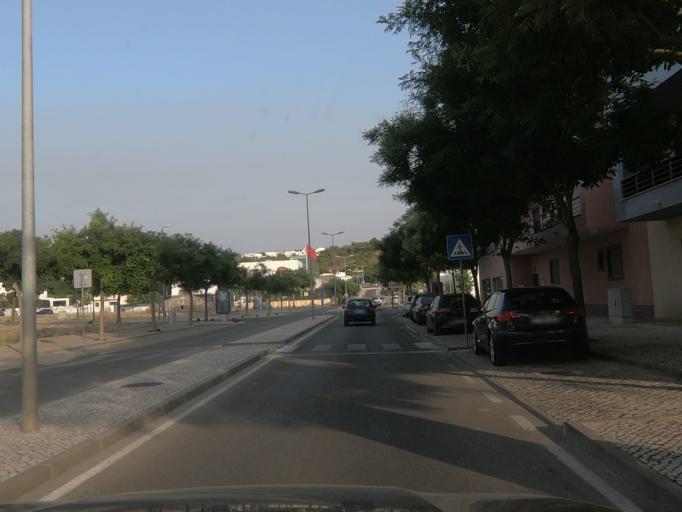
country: PT
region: Faro
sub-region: Loule
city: Loule
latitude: 37.1321
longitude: -8.0074
